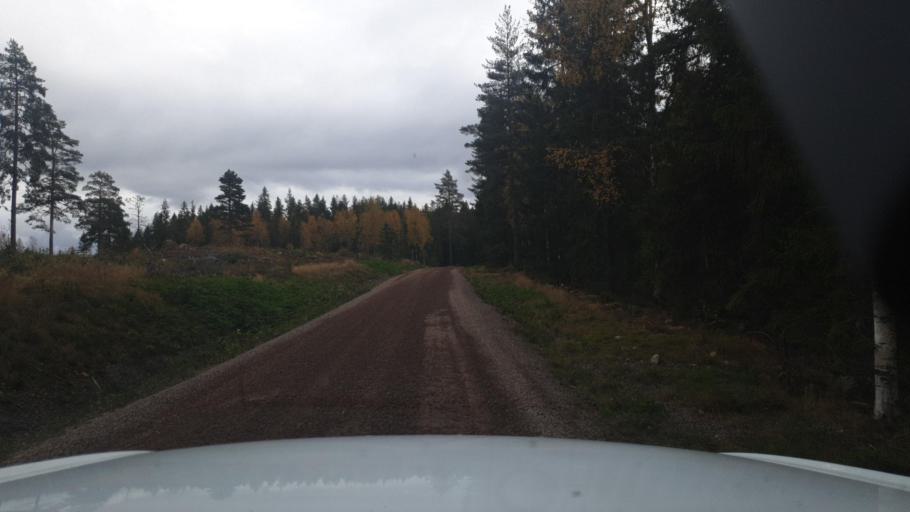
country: SE
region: Vaermland
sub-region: Eda Kommun
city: Charlottenberg
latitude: 60.0465
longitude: 12.5740
